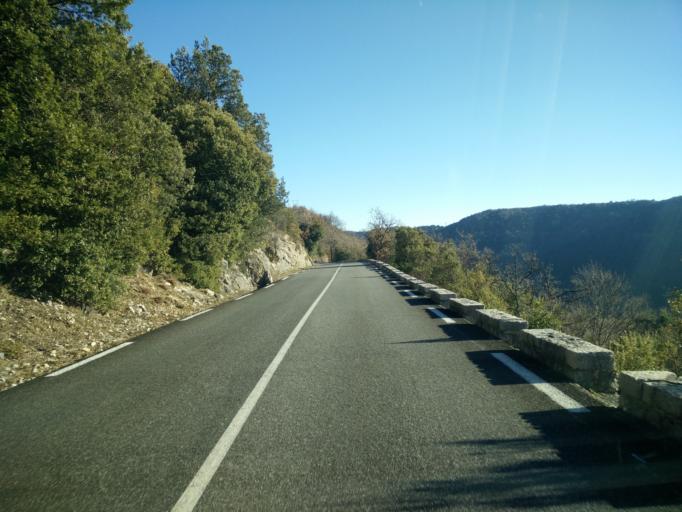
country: FR
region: Provence-Alpes-Cote d'Azur
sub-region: Departement des Alpes-Maritimes
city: Saint-Vallier-de-Thiey
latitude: 43.7217
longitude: 6.8221
